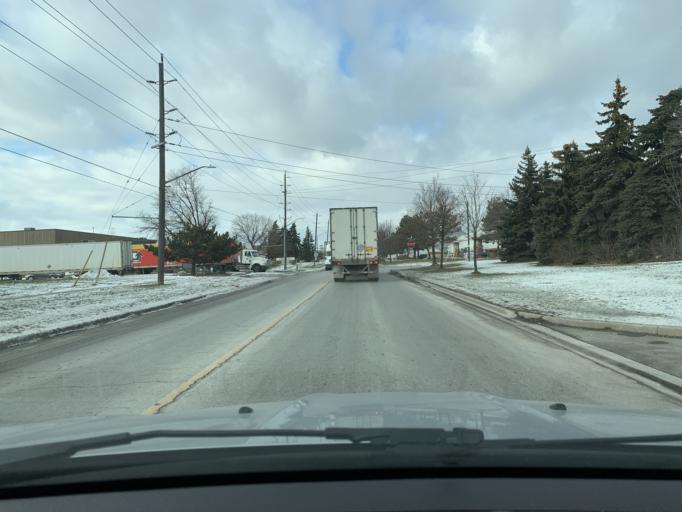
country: CA
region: Ontario
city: Brampton
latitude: 43.7280
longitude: -79.6811
